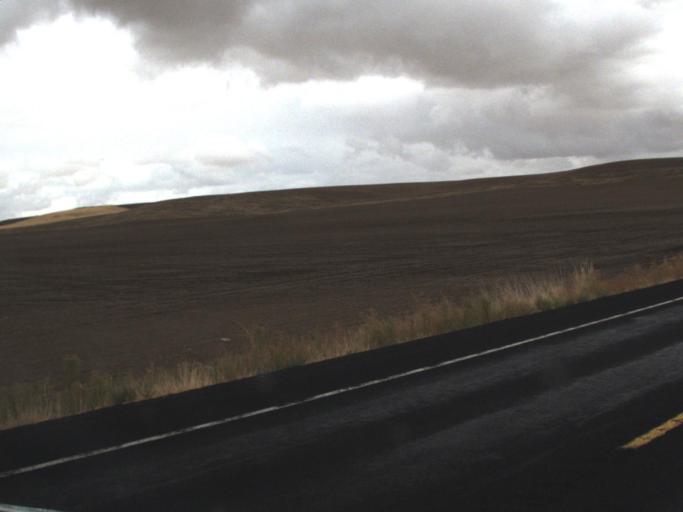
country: US
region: Washington
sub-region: Lincoln County
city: Davenport
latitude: 47.6442
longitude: -118.2093
